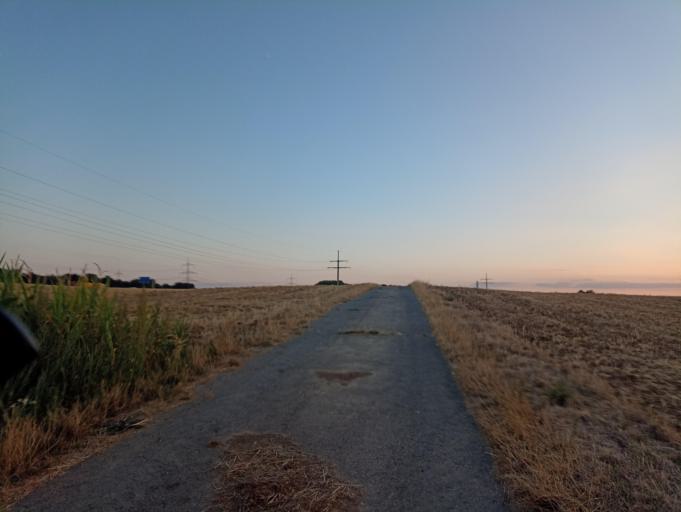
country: DE
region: Hesse
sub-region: Regierungsbezirk Darmstadt
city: Bad Homburg vor der Hoehe
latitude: 50.2059
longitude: 8.6503
